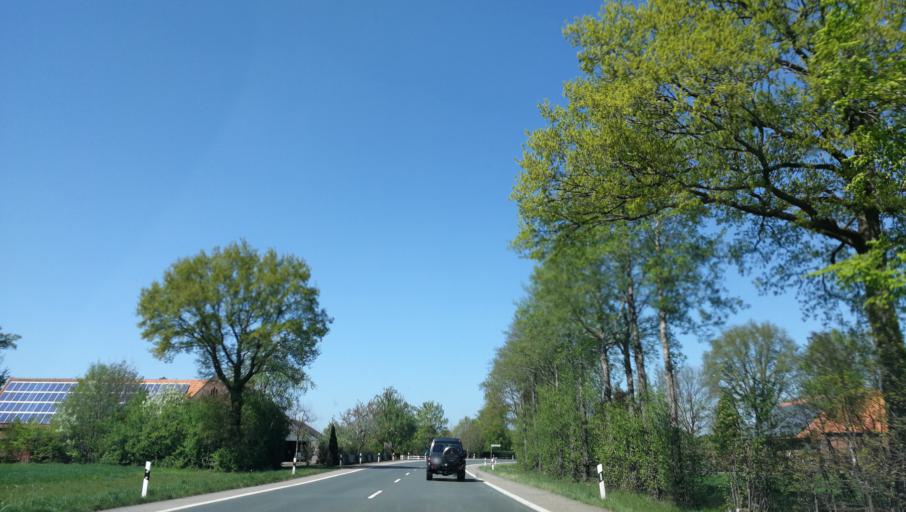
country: DE
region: North Rhine-Westphalia
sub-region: Regierungsbezirk Munster
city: Wettringen
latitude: 52.1938
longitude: 7.3249
